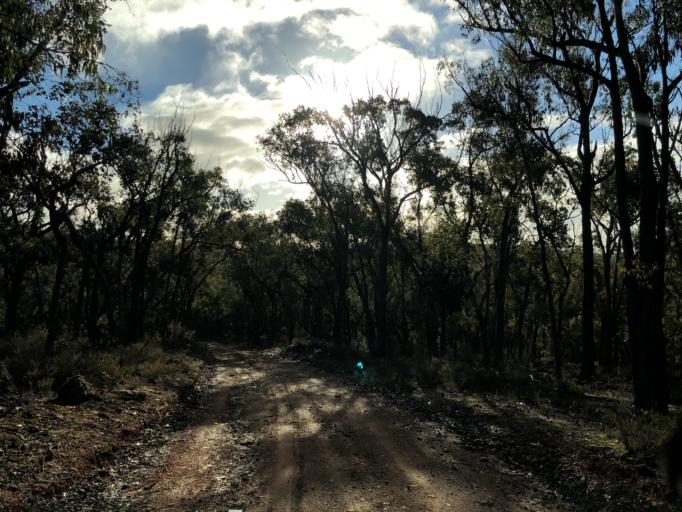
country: AU
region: Victoria
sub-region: Mount Alexander
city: Castlemaine
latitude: -37.2253
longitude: 144.2672
